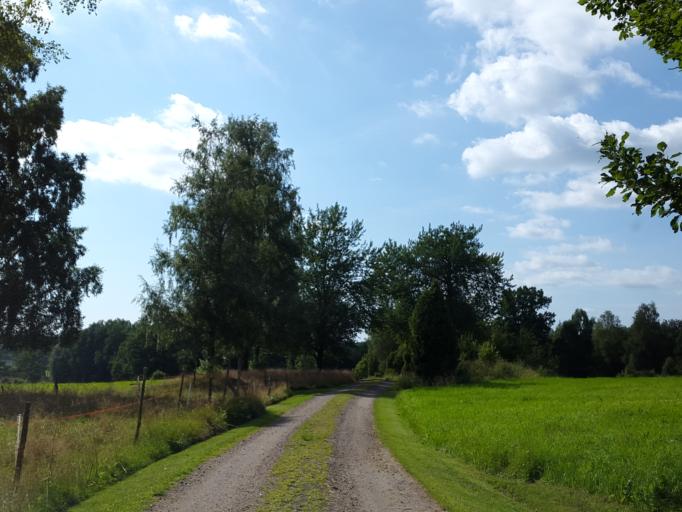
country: SE
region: Vaestra Goetaland
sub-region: Herrljunga Kommun
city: Herrljunga
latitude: 58.0222
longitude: 13.1233
